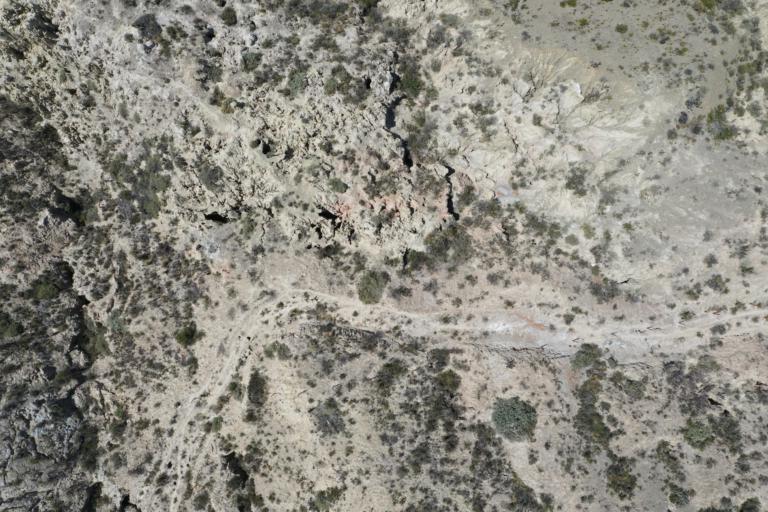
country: BO
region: La Paz
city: La Paz
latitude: -16.5609
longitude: -68.1141
